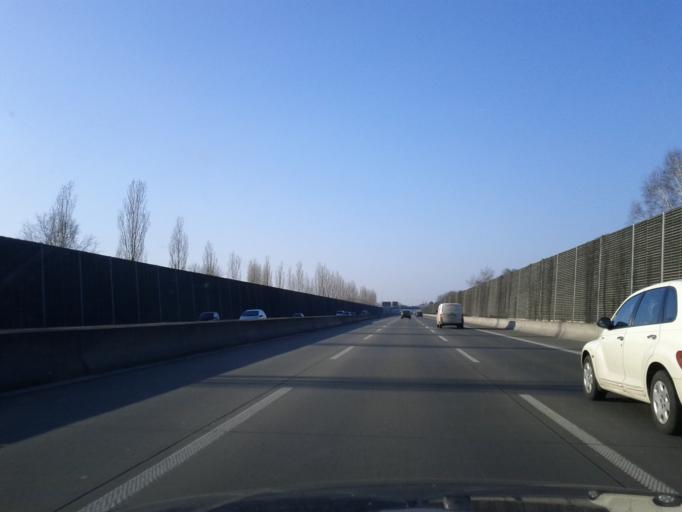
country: DE
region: Berlin
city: Rudow
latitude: 52.4393
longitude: 13.4869
